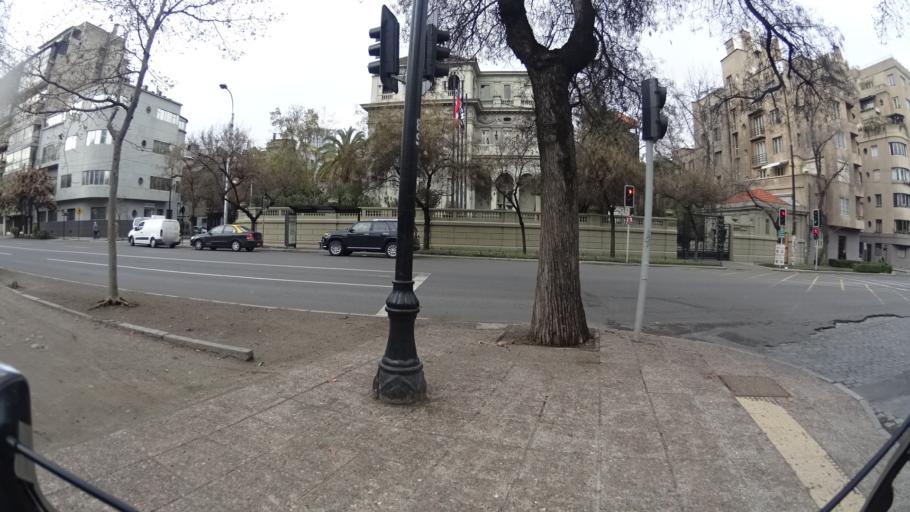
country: CL
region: Santiago Metropolitan
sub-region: Provincia de Santiago
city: Santiago
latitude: -33.4367
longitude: -70.6392
